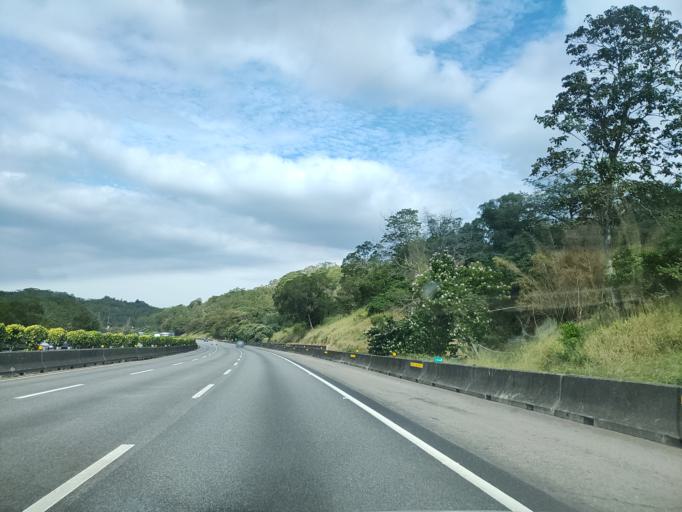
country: TW
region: Taiwan
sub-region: Miaoli
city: Miaoli
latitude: 24.6070
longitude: 120.8654
